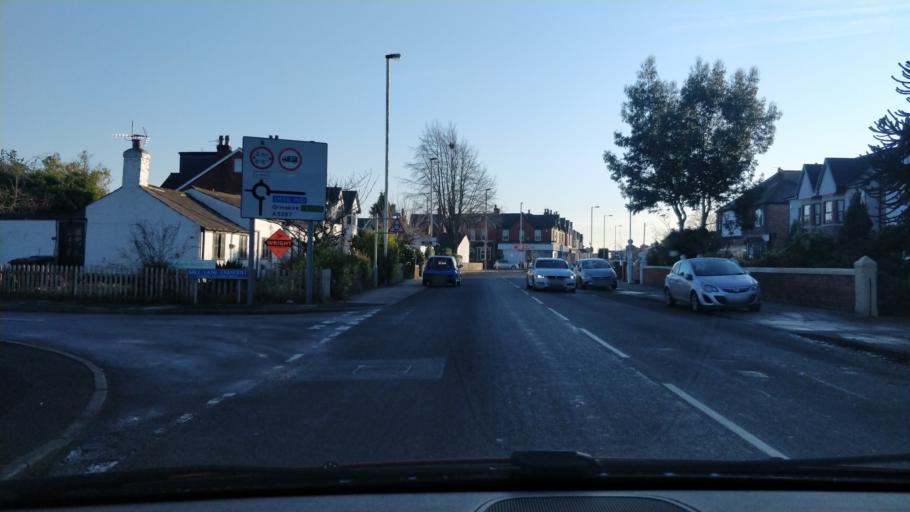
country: GB
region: England
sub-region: Sefton
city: Southport
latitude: 53.6552
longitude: -2.9654
